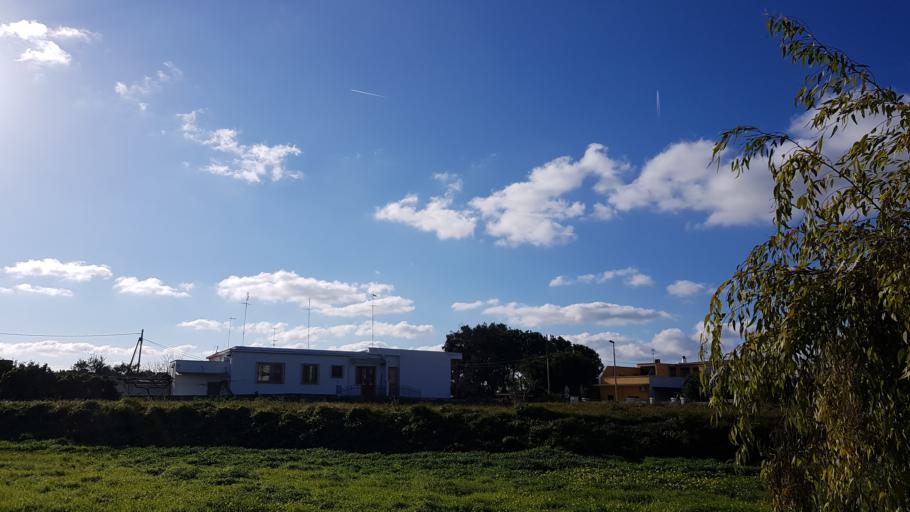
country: IT
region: Apulia
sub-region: Provincia di Brindisi
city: Materdomini
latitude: 40.6540
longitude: 17.9554
